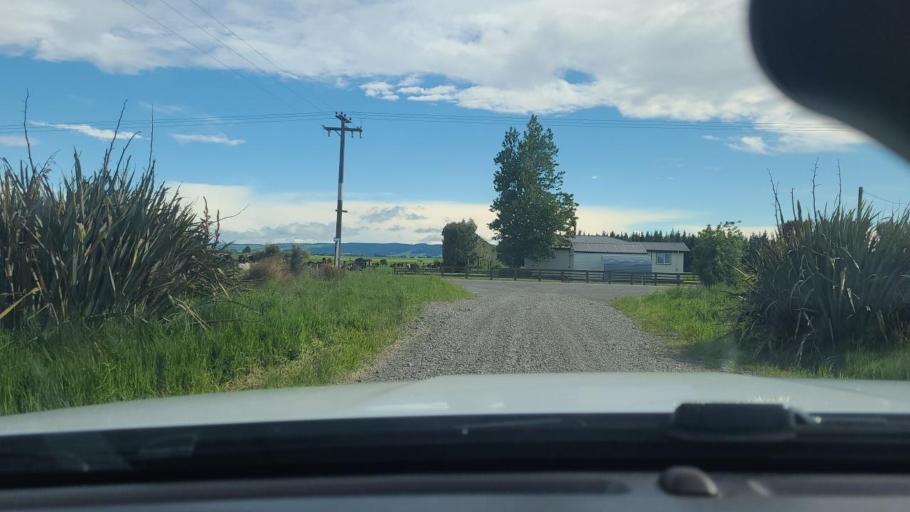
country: NZ
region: Southland
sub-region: Southland District
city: Winton
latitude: -46.0896
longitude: 168.2583
